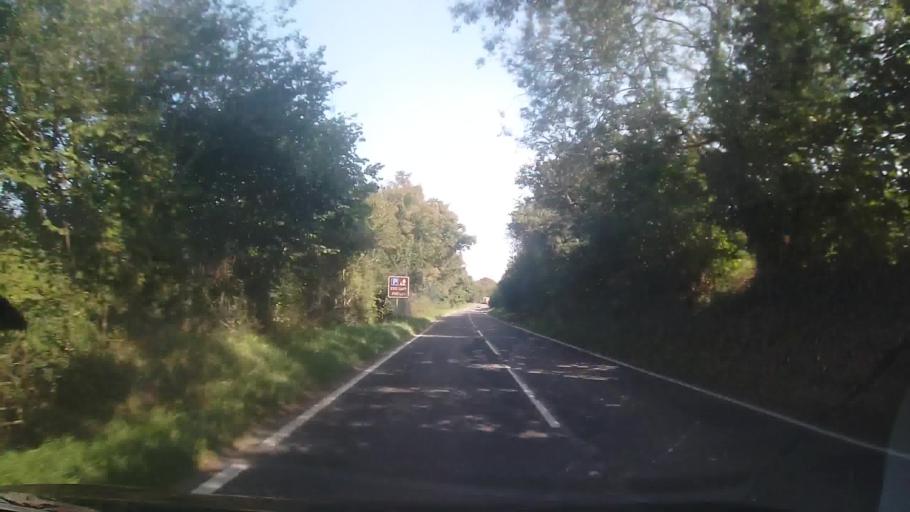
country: GB
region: Wales
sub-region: Pembrokeshire
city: Nevern
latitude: 52.0162
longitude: -4.7852
